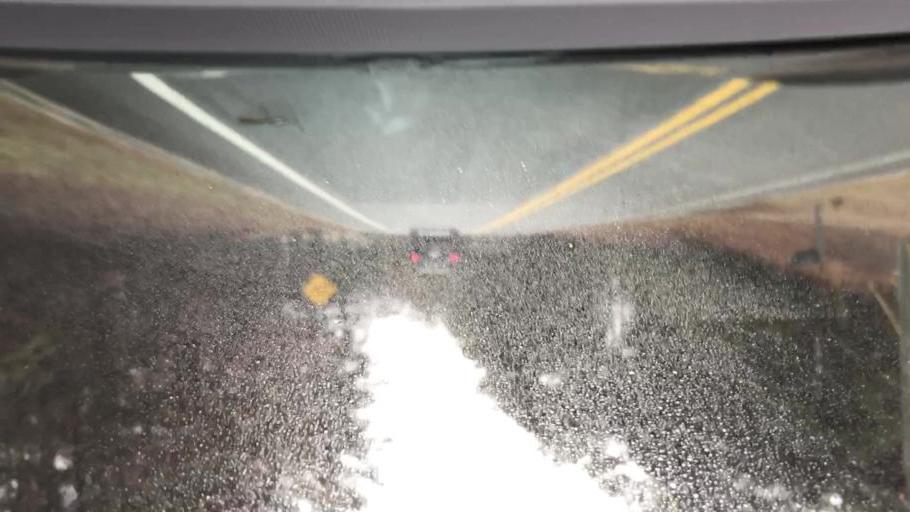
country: US
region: Georgia
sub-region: Gwinnett County
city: Buford
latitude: 34.1471
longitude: -84.0291
